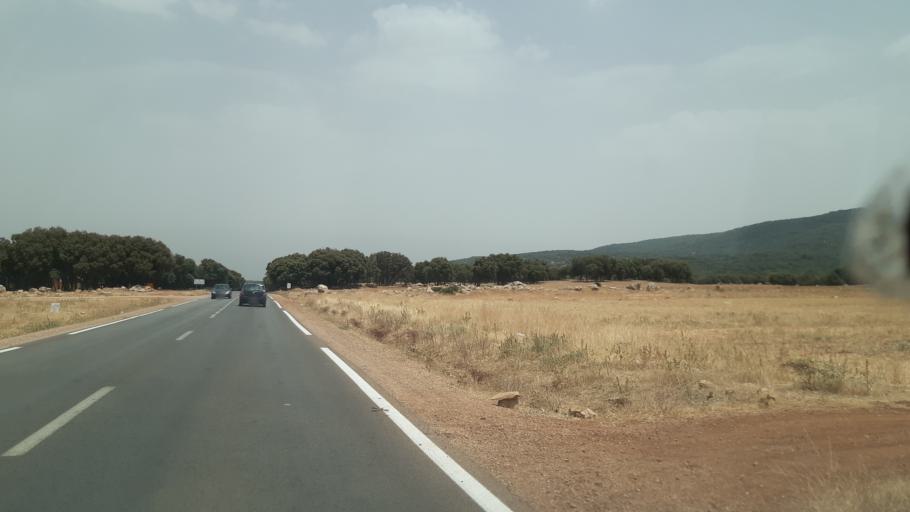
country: MA
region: Meknes-Tafilalet
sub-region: Ifrane
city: Ifrane
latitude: 33.6331
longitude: -5.0749
